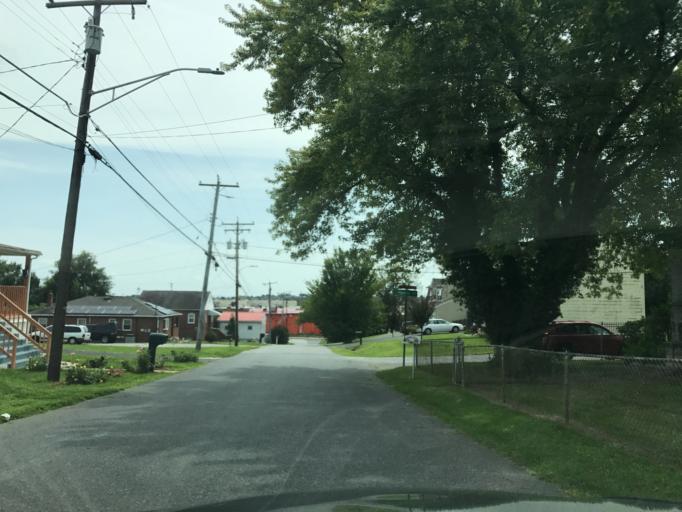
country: US
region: Maryland
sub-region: Baltimore County
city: Rosedale
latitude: 39.3136
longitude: -76.5282
